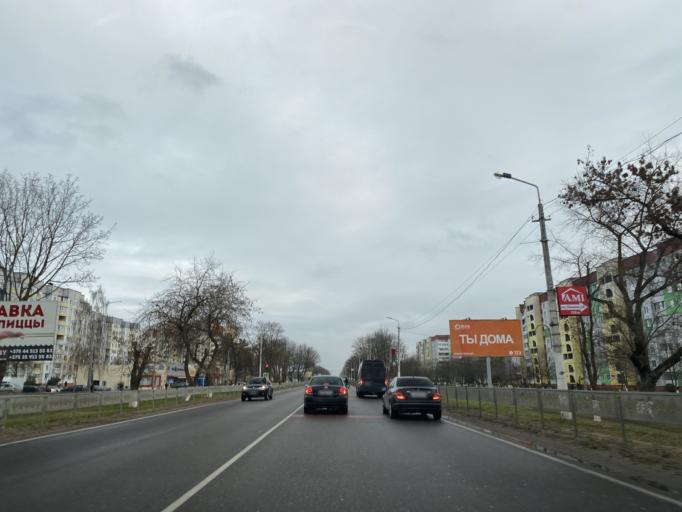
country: BY
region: Minsk
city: Horad Zhodzina
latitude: 54.0956
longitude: 28.2922
